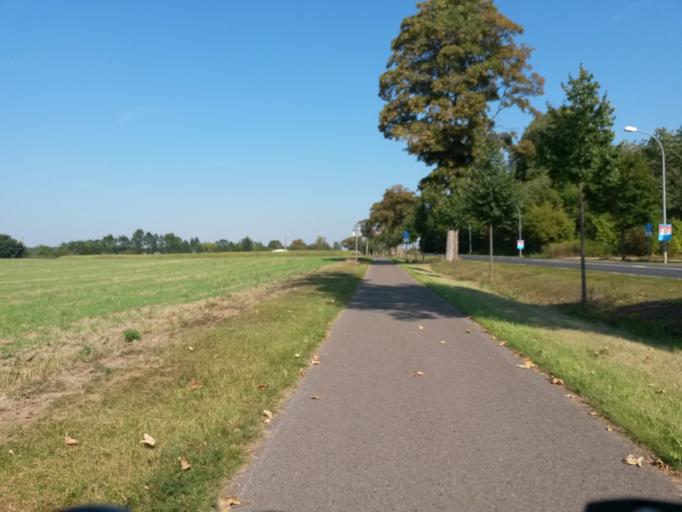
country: DE
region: Brandenburg
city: Templin
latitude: 53.1040
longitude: 13.4777
